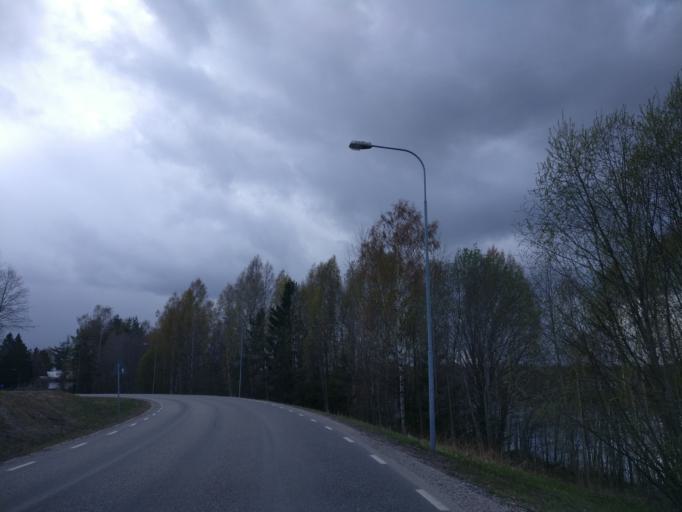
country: SE
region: Vaesternorrland
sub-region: Sundsvalls Kommun
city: Skottsund
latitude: 62.2944
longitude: 17.3875
